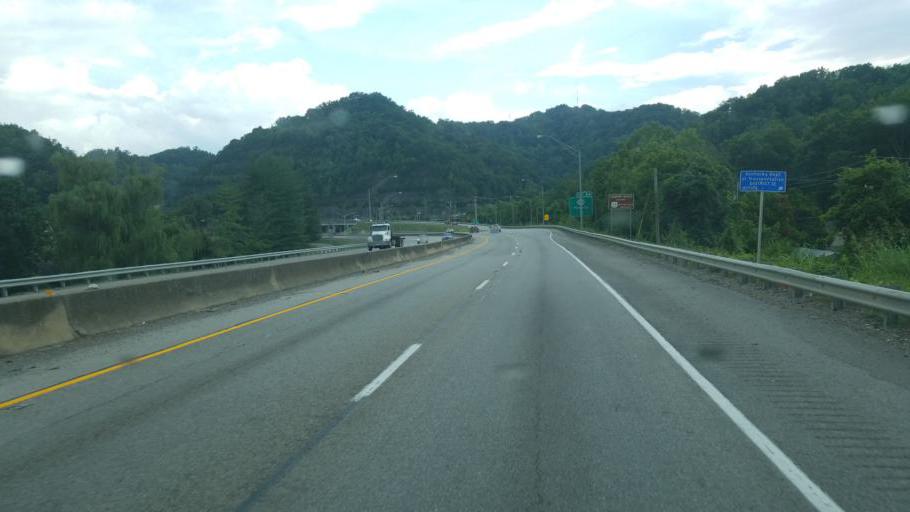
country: US
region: Kentucky
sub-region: Pike County
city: Pikeville
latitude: 37.4838
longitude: -82.5432
